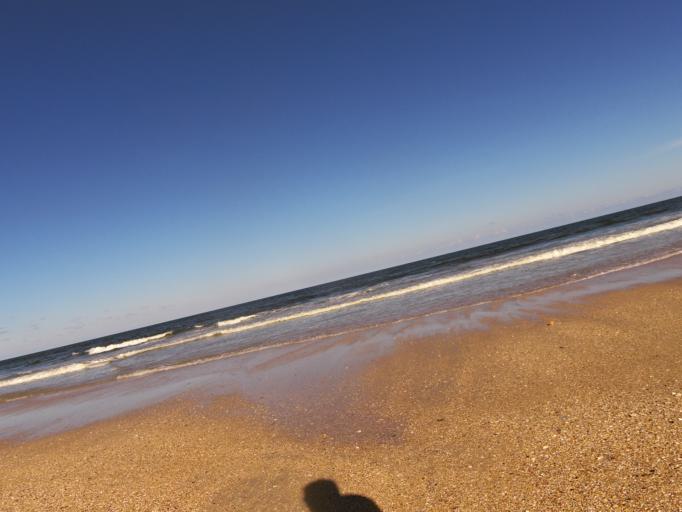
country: US
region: Florida
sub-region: Saint Johns County
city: Sawgrass
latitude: 30.1768
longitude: -81.3596
